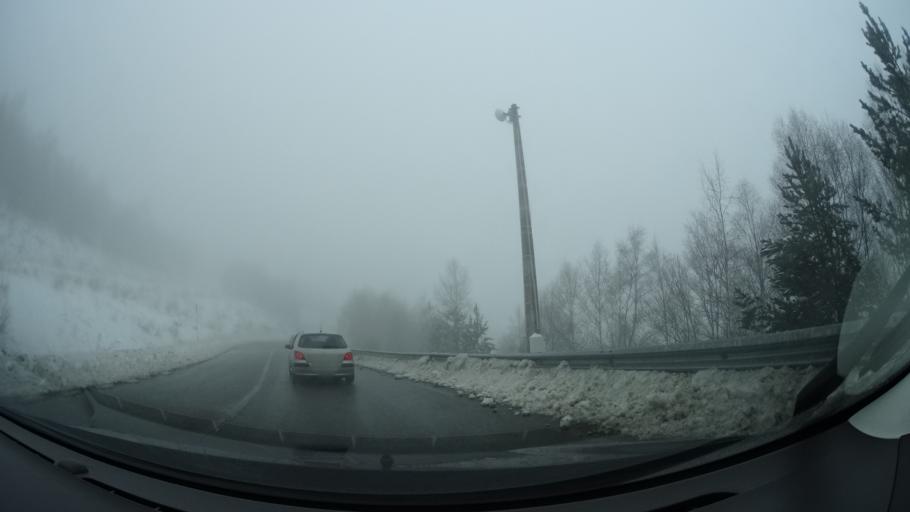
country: AD
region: Encamp
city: Pas de la Casa
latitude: 42.5766
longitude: 1.7925
